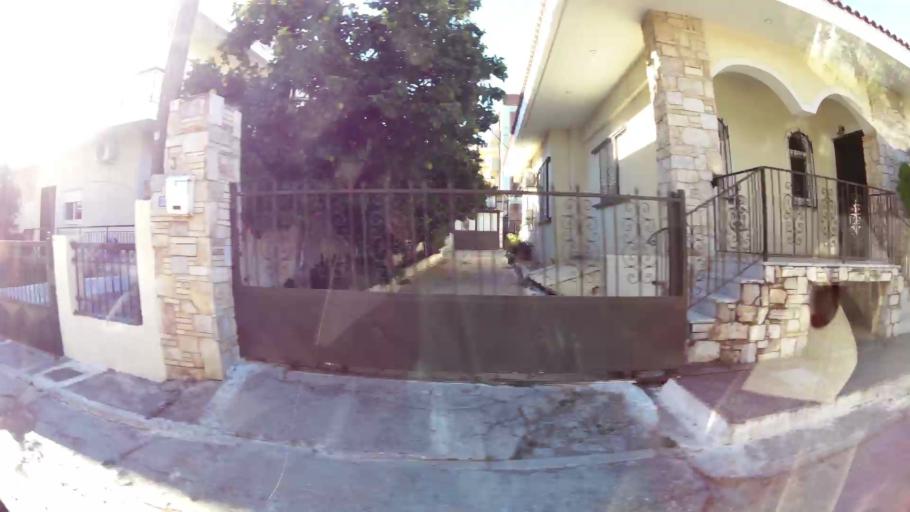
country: GR
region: Attica
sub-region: Nomarchia Anatolikis Attikis
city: Koropi
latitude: 37.9007
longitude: 23.8631
